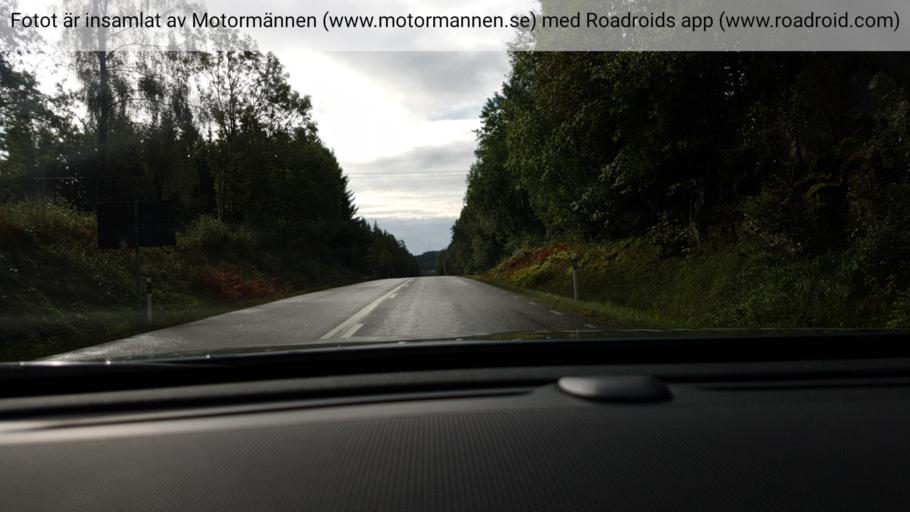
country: SE
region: Vaestra Goetaland
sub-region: Harryda Kommun
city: Ravlanda
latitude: 57.5639
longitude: 12.5136
